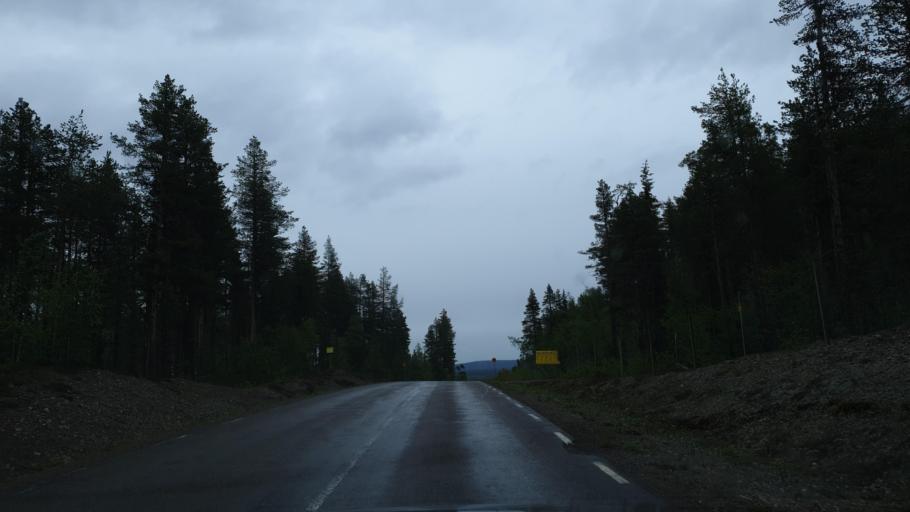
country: SE
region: Norrbotten
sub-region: Gallivare Kommun
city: Malmberget
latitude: 67.8932
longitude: 21.0524
